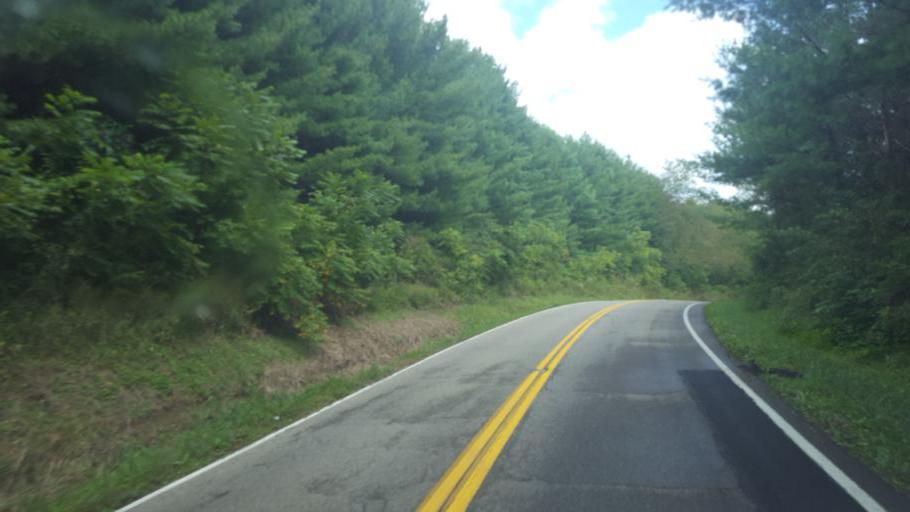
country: US
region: Ohio
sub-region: Jackson County
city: Oak Hill
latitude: 38.8866
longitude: -82.6872
